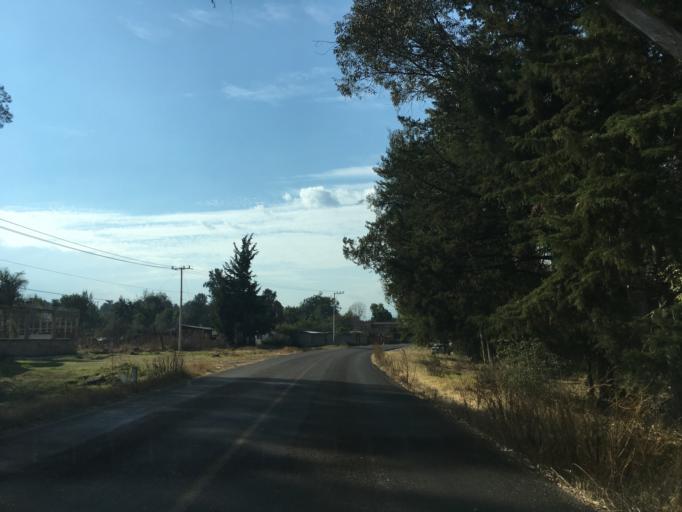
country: MX
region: Michoacan
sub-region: Patzcuaro
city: Santa Ana Chapitiro
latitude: 19.5285
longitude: -101.6505
